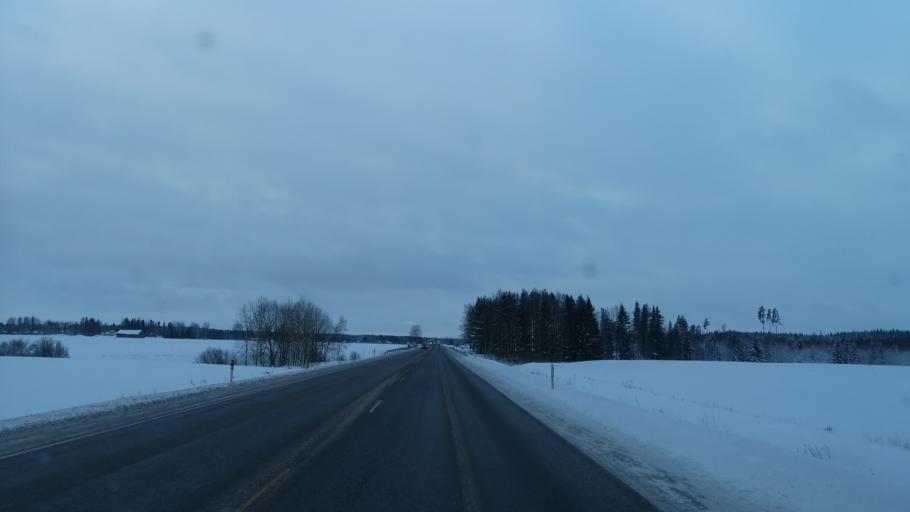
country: FI
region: Varsinais-Suomi
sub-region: Loimaa
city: Loimaa
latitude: 60.8945
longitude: 23.1172
